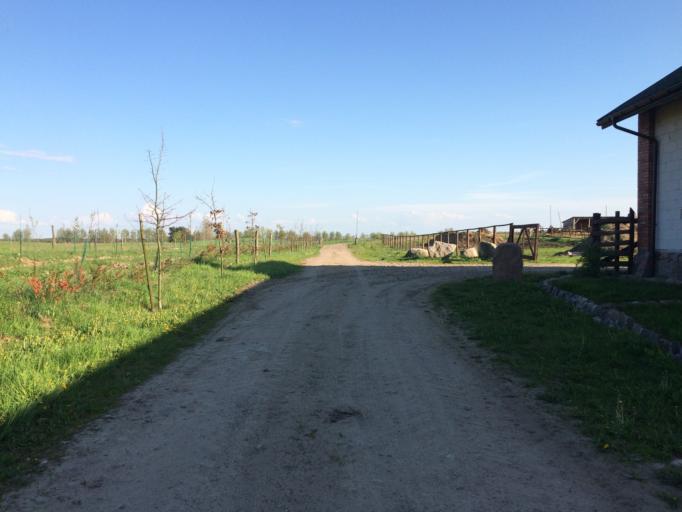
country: PL
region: Warmian-Masurian Voivodeship
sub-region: Powiat dzialdowski
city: Rybno
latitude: 53.4195
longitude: 19.9124
